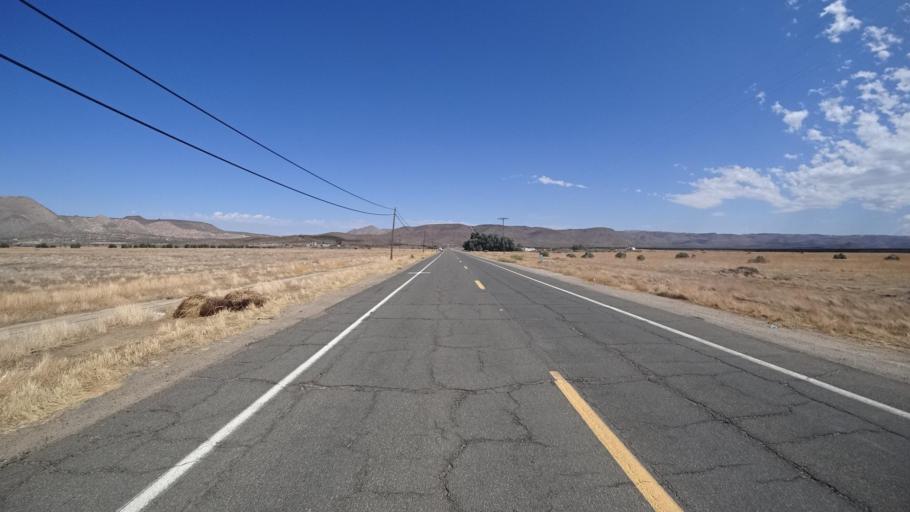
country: MX
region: Baja California
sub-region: Tecate
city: Cereso del Hongo
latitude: 32.6177
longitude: -116.1813
